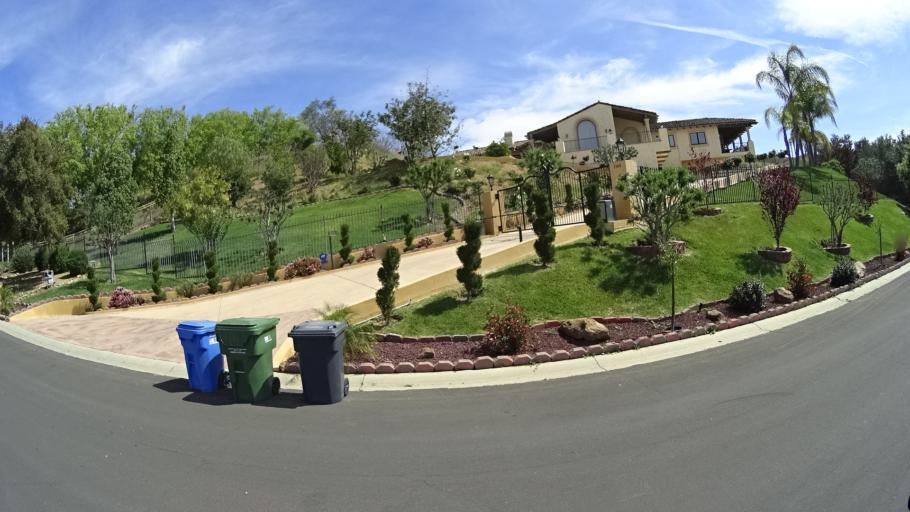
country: US
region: California
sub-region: Ventura County
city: Thousand Oaks
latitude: 34.2004
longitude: -118.8139
